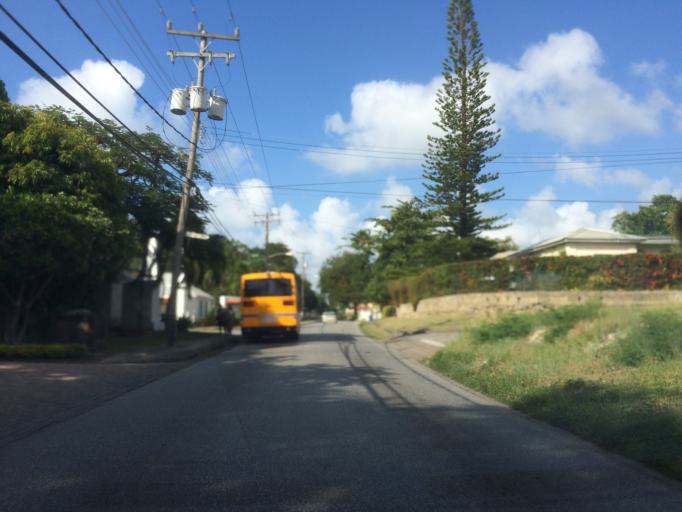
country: BB
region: Saint James
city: Holetown
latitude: 13.1990
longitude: -59.6395
